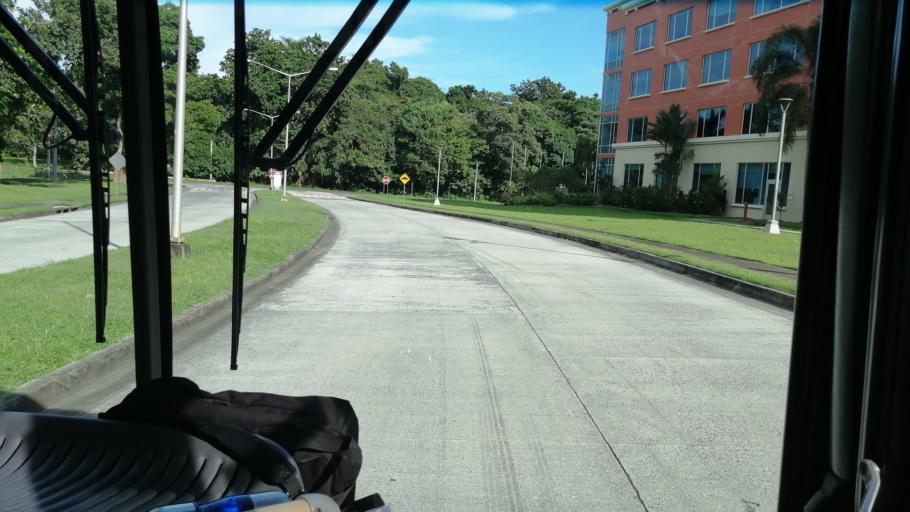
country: PA
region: Panama
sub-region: Distrito de Panama
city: Ancon
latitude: 8.9285
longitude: -79.5932
